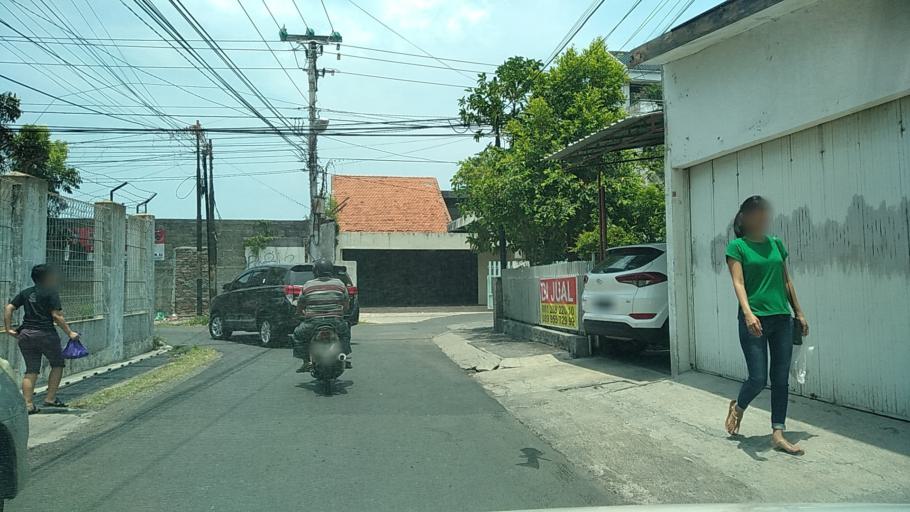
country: ID
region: Central Java
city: Semarang
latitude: -6.9746
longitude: 110.4170
